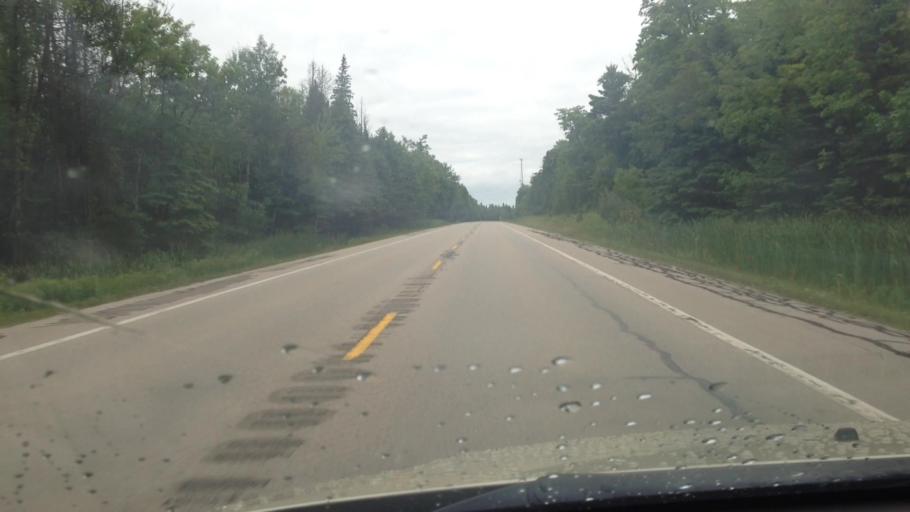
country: US
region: Michigan
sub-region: Menominee County
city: Menominee
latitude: 45.3992
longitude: -87.3651
